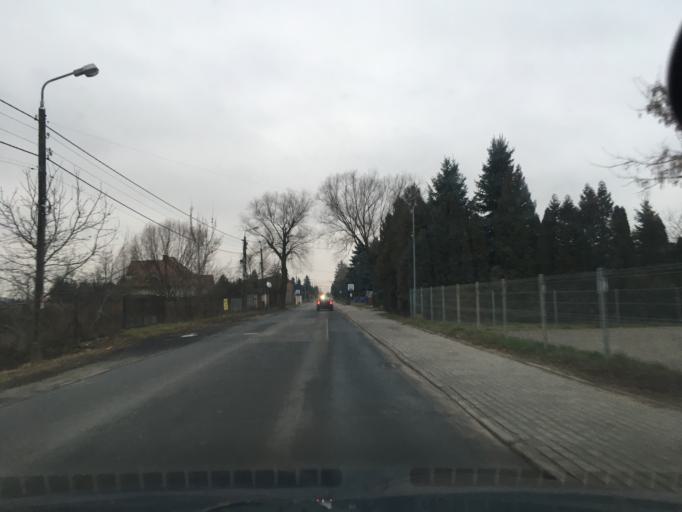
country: PL
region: Masovian Voivodeship
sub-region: Powiat piaseczynski
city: Mysiadlo
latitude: 52.1251
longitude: 20.9796
